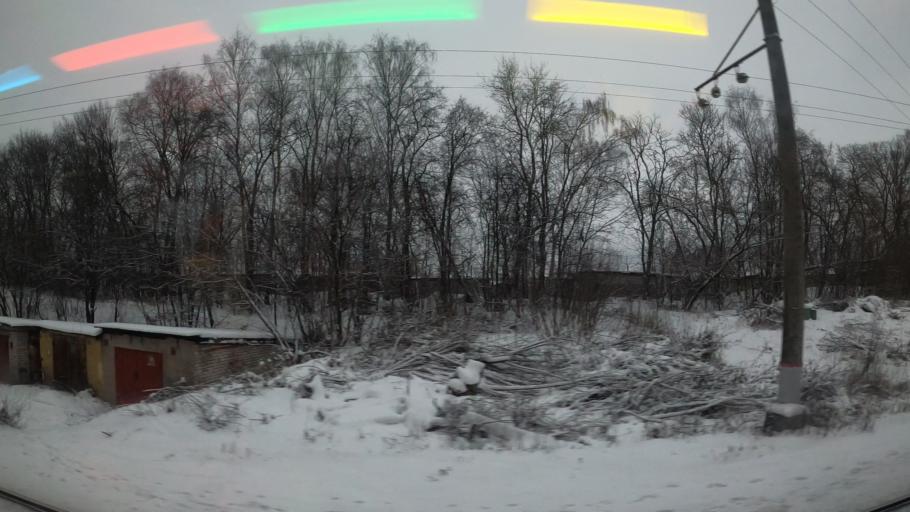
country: RU
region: Vladimir
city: Aleksandrov
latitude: 56.4059
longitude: 38.7283
